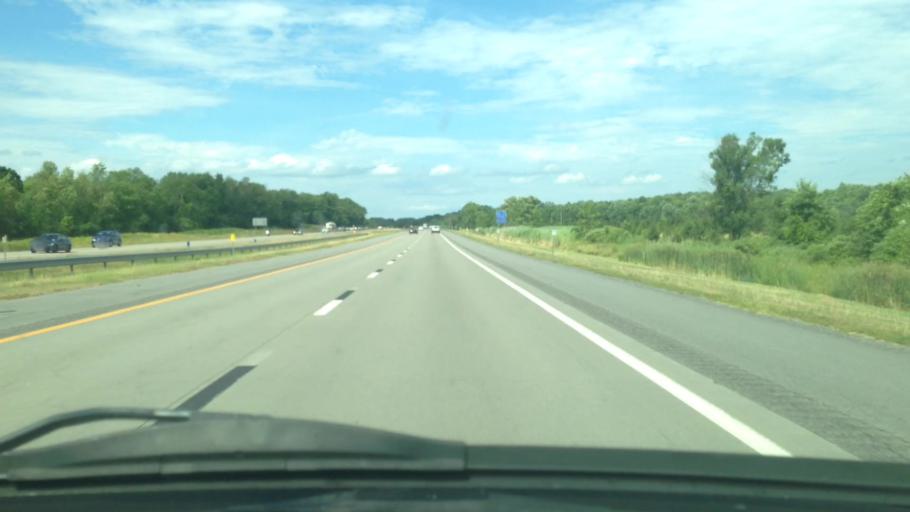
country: US
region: New York
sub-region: Onondaga County
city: Jordan
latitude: 43.0749
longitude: -76.4977
